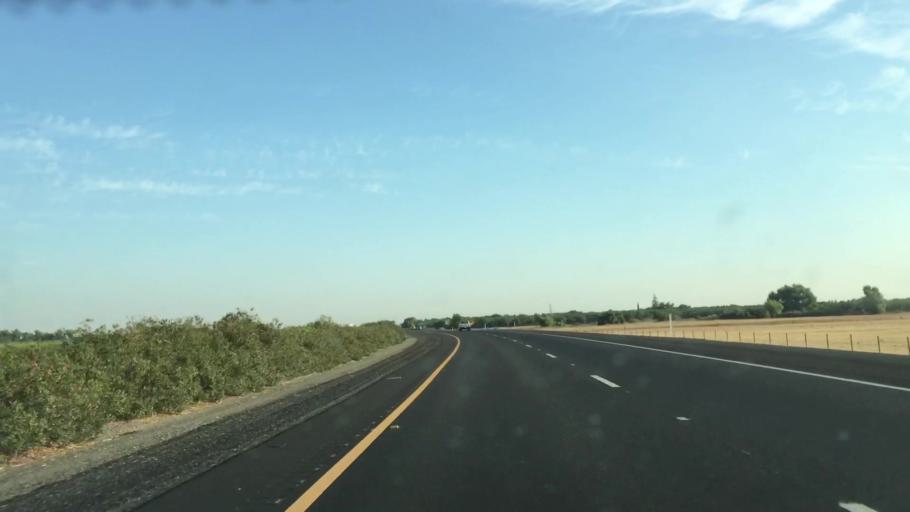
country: US
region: California
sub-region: Glenn County
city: Willows
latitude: 39.6300
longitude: -122.2042
